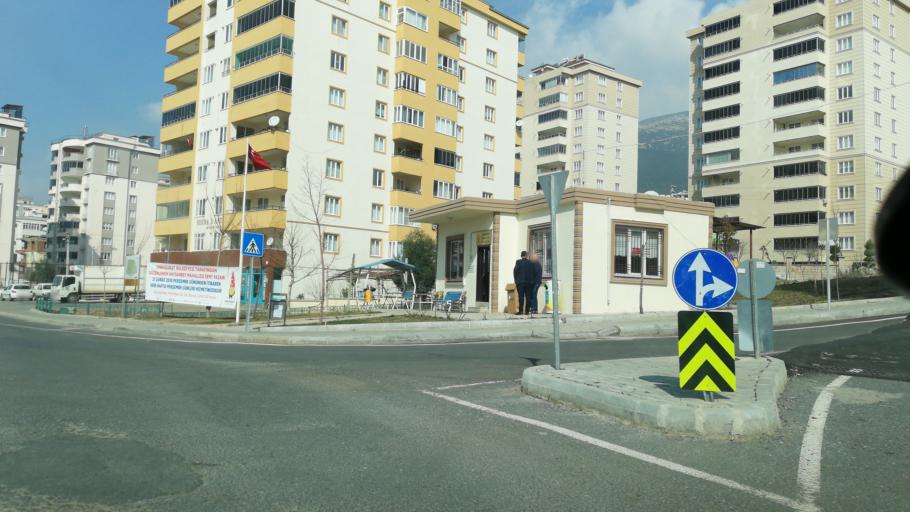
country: TR
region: Kahramanmaras
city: Kahramanmaras
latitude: 37.5878
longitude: 36.8661
